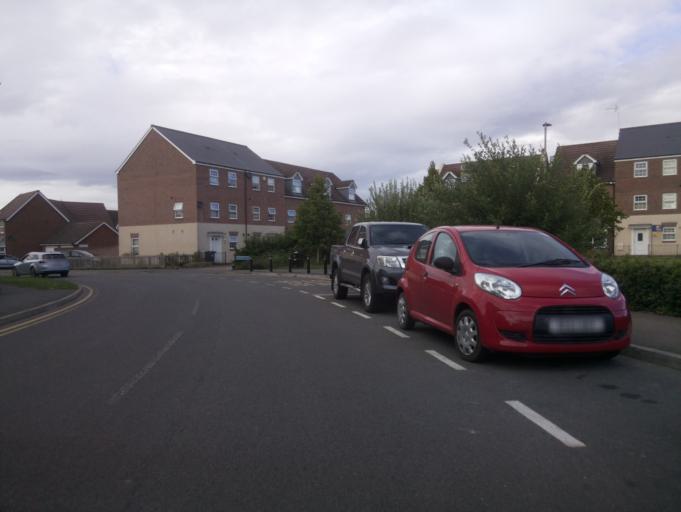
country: GB
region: England
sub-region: Gloucestershire
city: Gloucester
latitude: 51.8219
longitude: -2.2629
